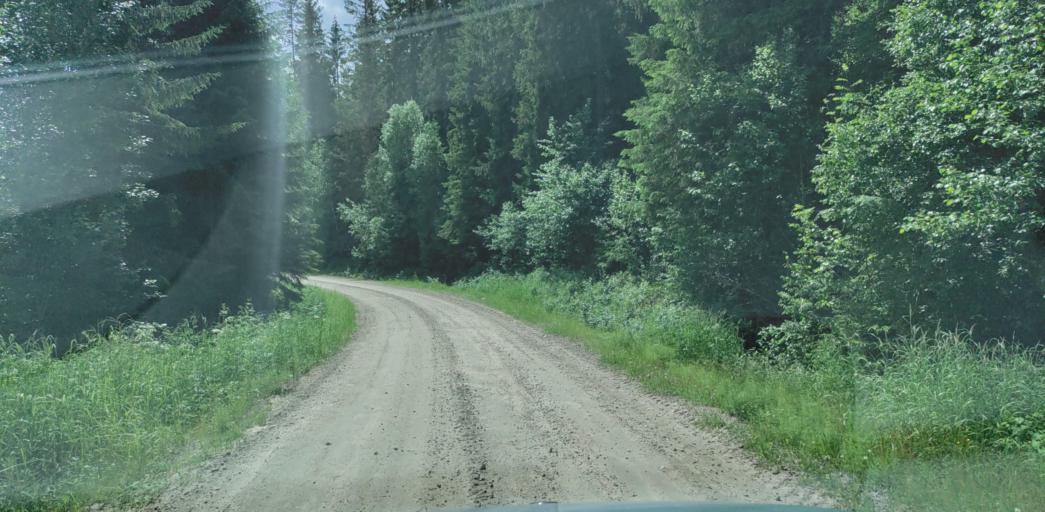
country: SE
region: Vaermland
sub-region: Sunne Kommun
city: Sunne
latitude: 60.0493
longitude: 13.2590
